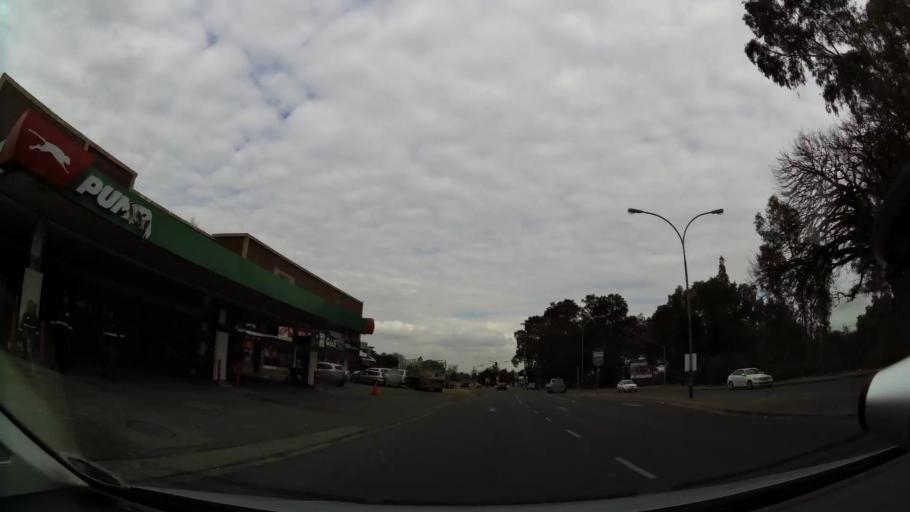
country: ZA
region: Orange Free State
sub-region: Mangaung Metropolitan Municipality
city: Bloemfontein
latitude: -29.0958
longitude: 26.2033
